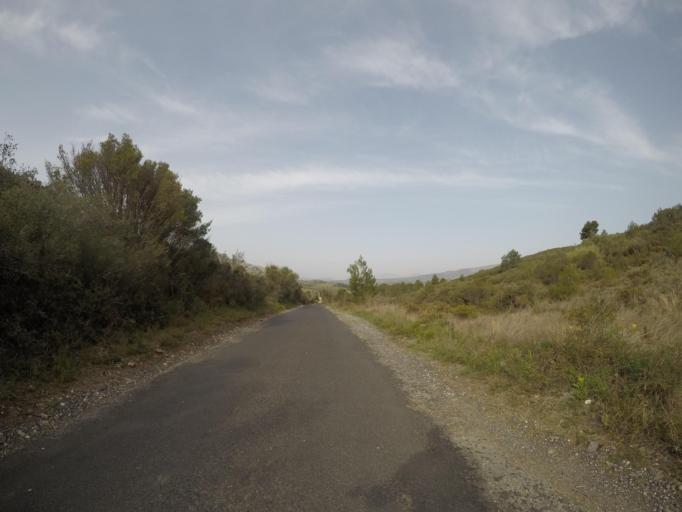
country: FR
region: Languedoc-Roussillon
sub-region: Departement des Pyrenees-Orientales
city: Baixas
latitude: 42.7712
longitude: 2.8024
